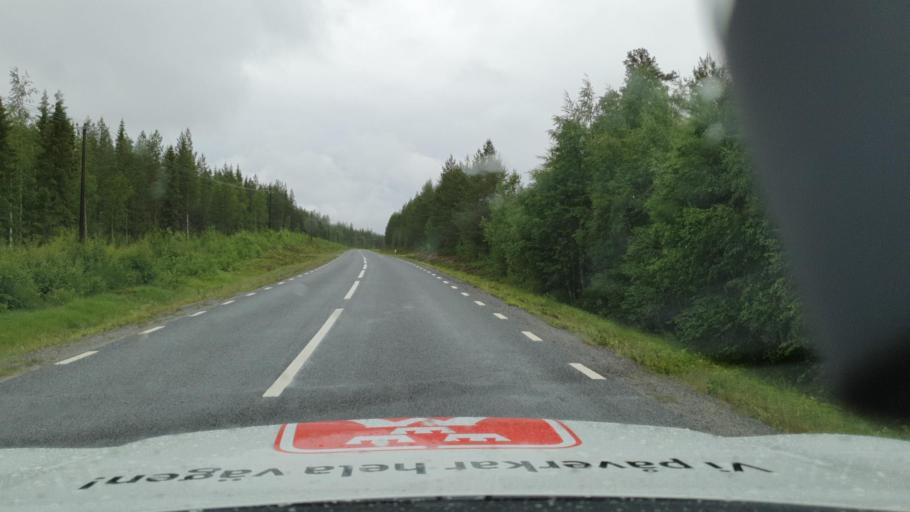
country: SE
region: Vaesterbotten
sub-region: Asele Kommun
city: Asele
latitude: 63.9318
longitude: 17.2673
